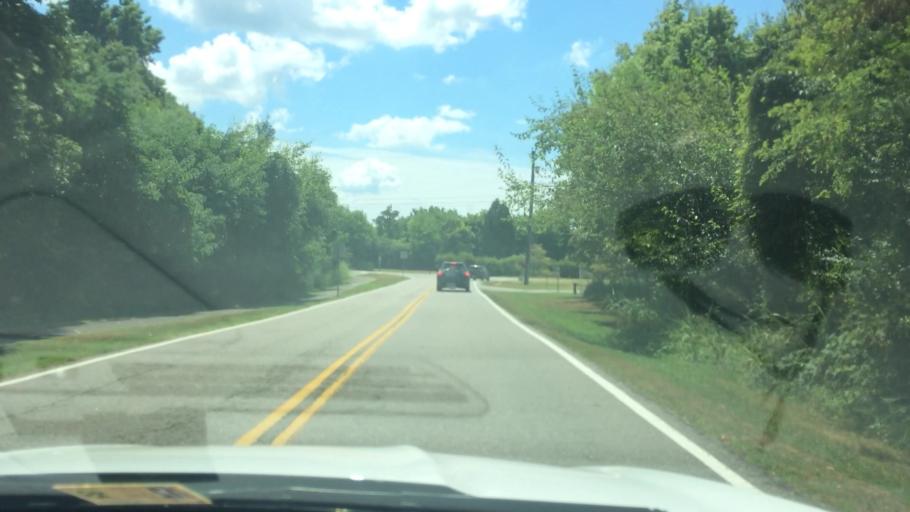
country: US
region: Virginia
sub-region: King William County
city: West Point
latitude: 37.5399
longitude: -76.7941
